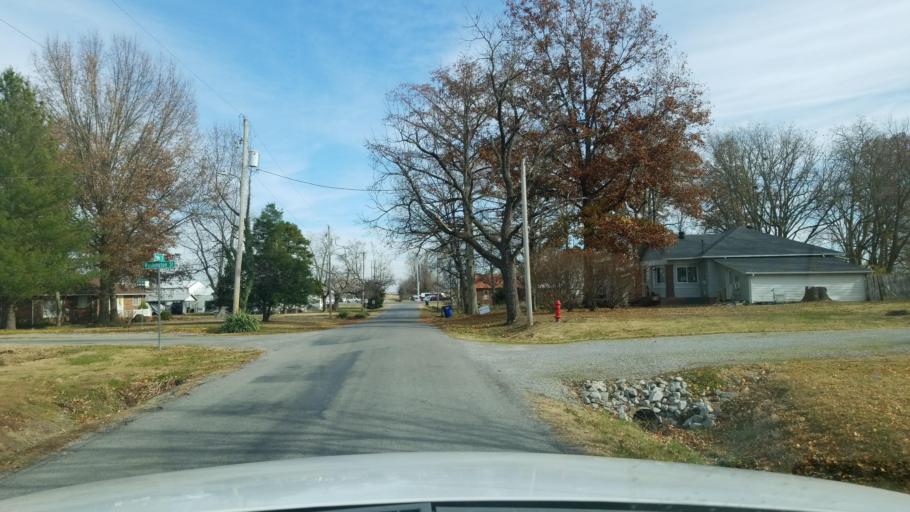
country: US
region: Illinois
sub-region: Saline County
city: Harrisburg
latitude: 37.7638
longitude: -88.5145
